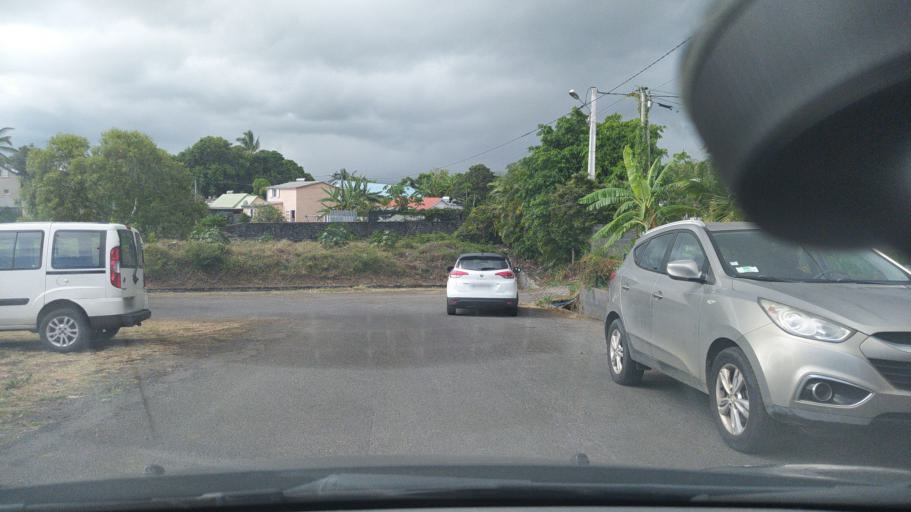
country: RE
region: Reunion
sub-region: Reunion
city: Saint-Pierre
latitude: -21.3107
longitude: 55.4723
